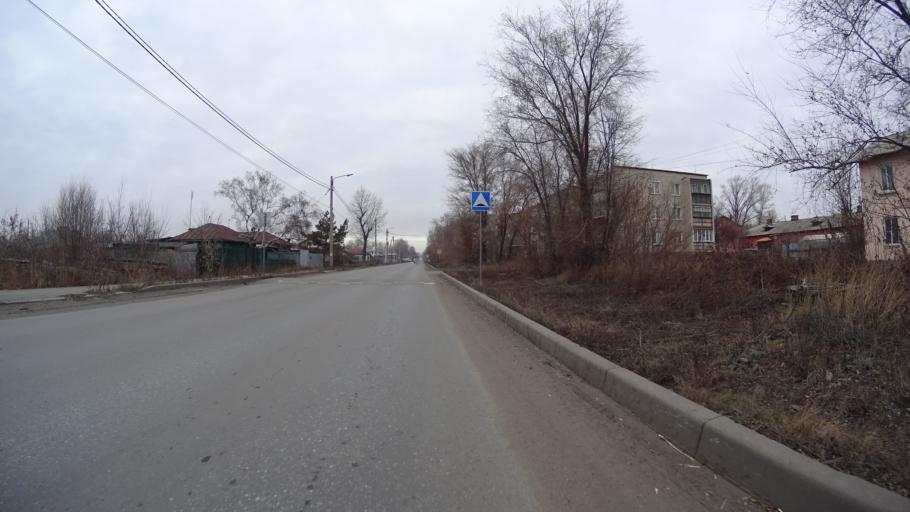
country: RU
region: Chelyabinsk
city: Troitsk
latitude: 54.1083
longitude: 61.5719
